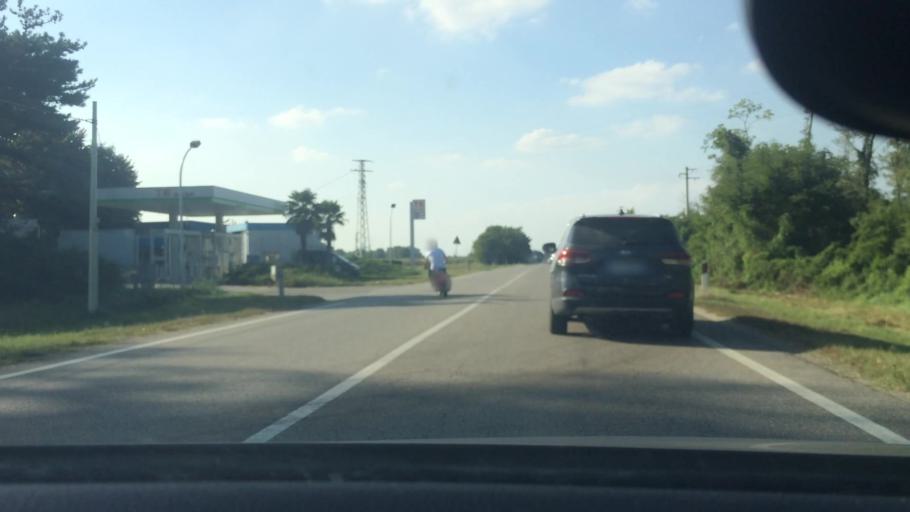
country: IT
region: Lombardy
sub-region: Citta metropolitana di Milano
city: Arconate
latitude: 45.5319
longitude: 8.8319
